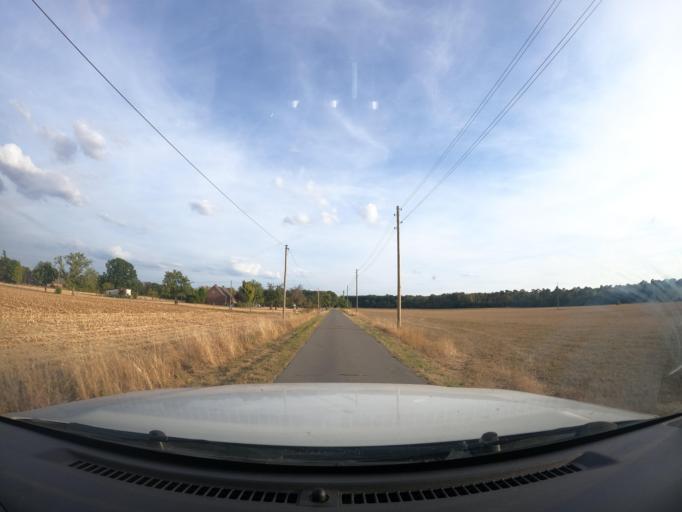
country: DE
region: North Rhine-Westphalia
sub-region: Regierungsbezirk Dusseldorf
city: Hamminkeln
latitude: 51.7054
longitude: 6.5688
